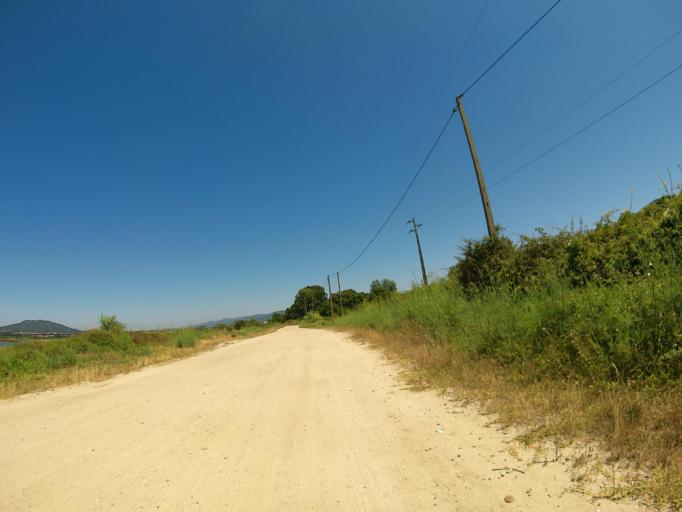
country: PT
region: Viana do Castelo
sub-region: Viana do Castelo
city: Meadela
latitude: 41.6879
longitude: -8.7997
